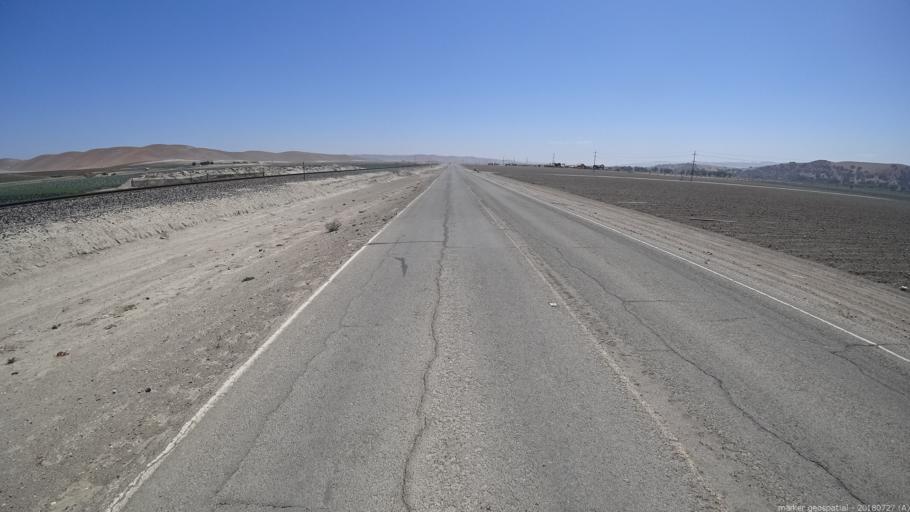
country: US
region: California
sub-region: Monterey County
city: King City
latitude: 36.0975
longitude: -120.9672
